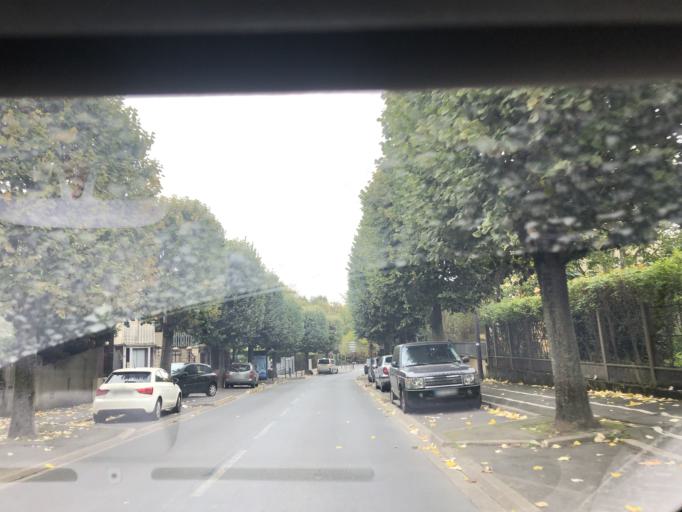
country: FR
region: Ile-de-France
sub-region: Departement du Val-de-Marne
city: Vitry-sur-Seine
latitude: 48.7983
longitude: 2.3914
